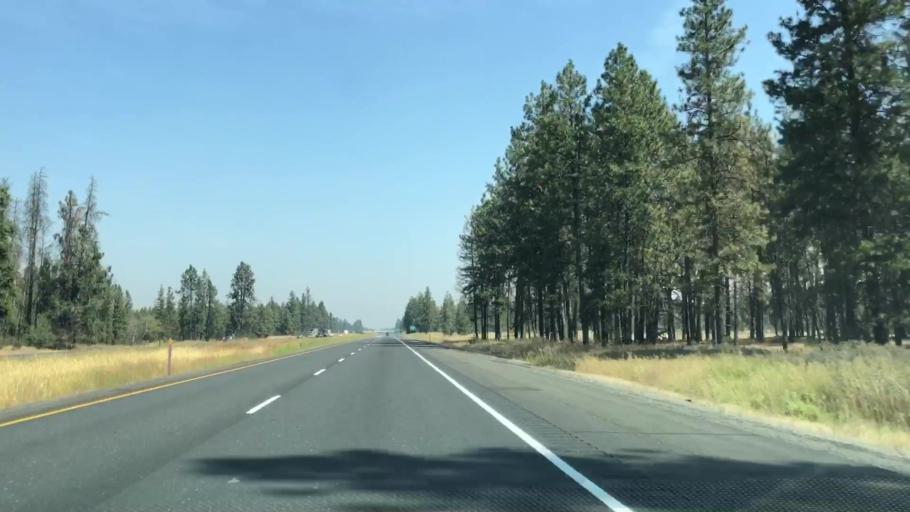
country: US
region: Washington
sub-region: Spokane County
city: Medical Lake
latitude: 47.4938
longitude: -117.7058
